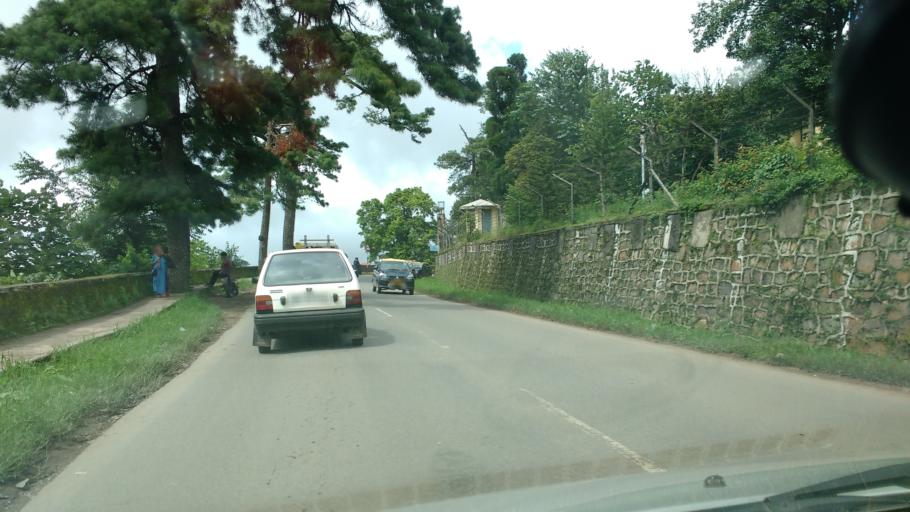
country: IN
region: Meghalaya
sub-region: East Khasi Hills
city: Shillong
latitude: 25.5673
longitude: 91.8559
